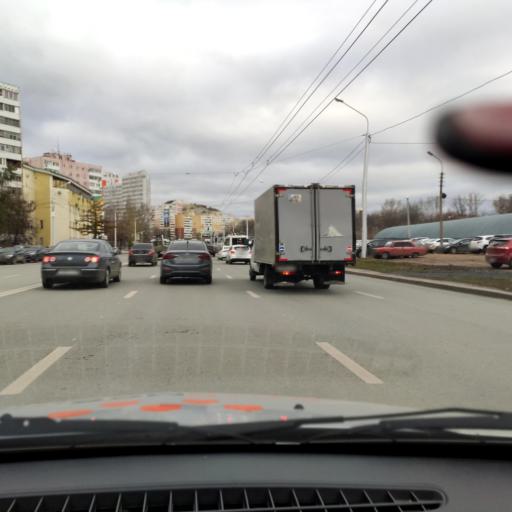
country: RU
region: Bashkortostan
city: Ufa
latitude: 54.7581
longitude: 56.0244
